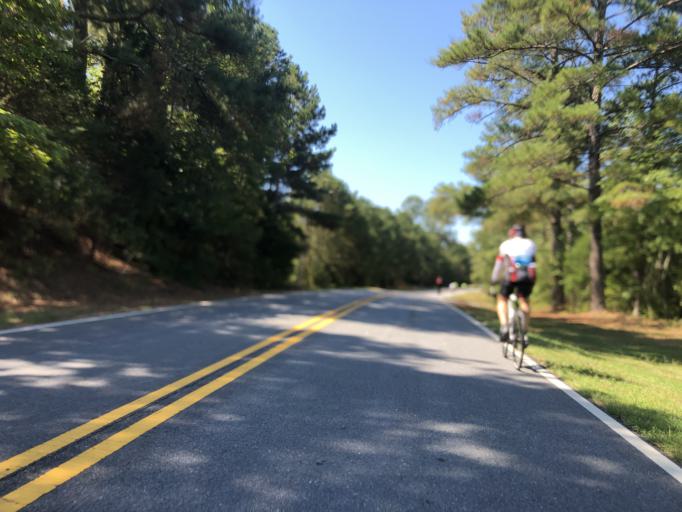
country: US
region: Georgia
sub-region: Coweta County
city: Newnan
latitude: 33.3953
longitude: -84.9623
